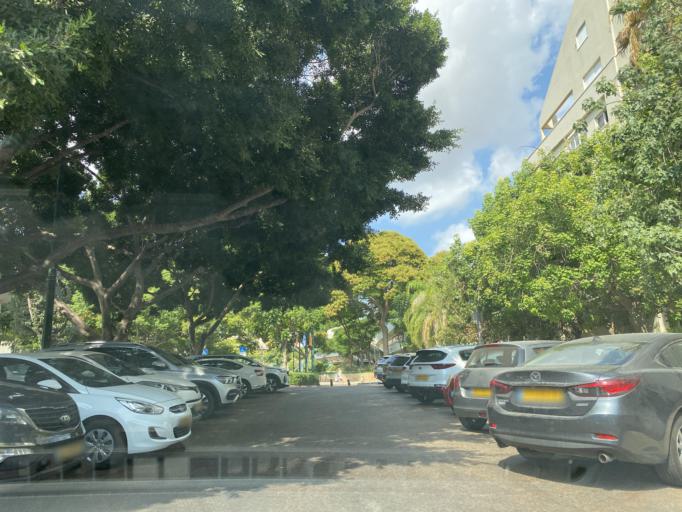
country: IL
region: Central District
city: Kfar Saba
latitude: 32.1773
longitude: 34.9069
